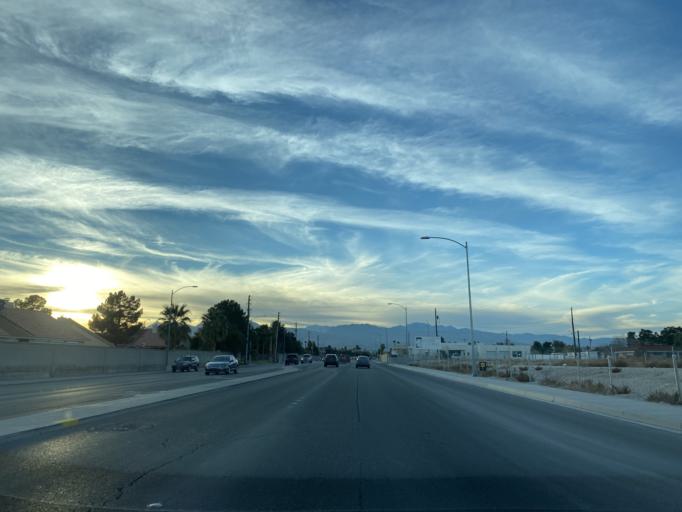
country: US
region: Nevada
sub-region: Clark County
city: Las Vegas
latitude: 36.2611
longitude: -115.2218
